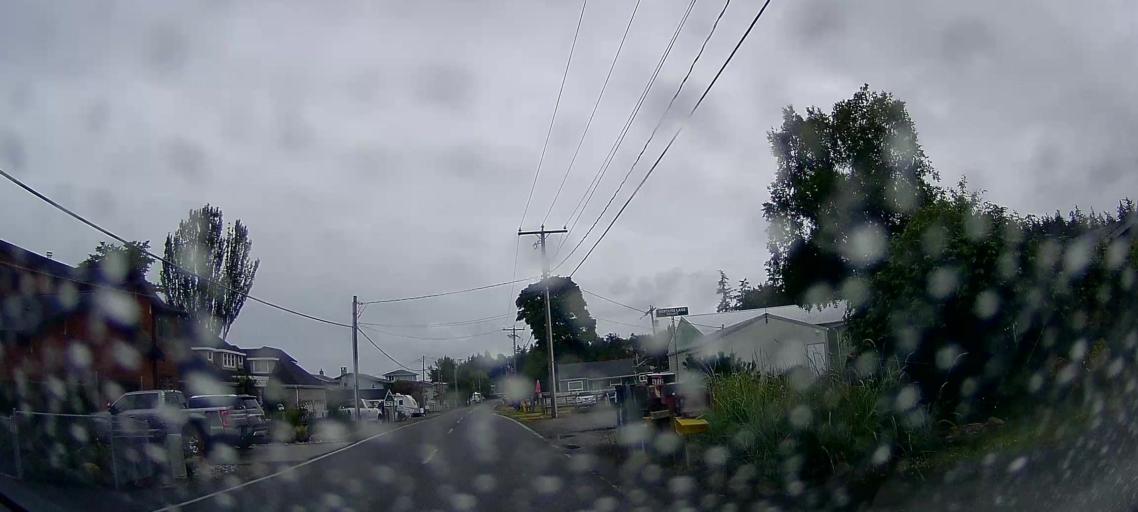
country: US
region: Washington
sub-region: Whatcom County
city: Birch Bay
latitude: 48.8137
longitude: -122.7083
